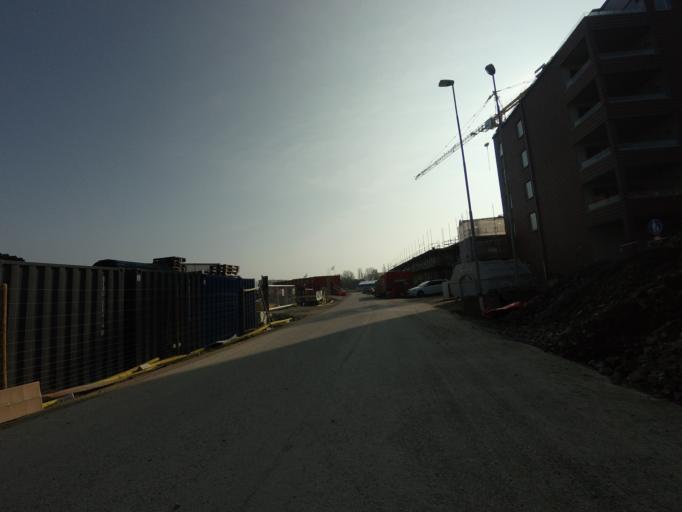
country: SE
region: Skane
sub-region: Malmo
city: Bunkeflostrand
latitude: 55.5628
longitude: 12.9806
